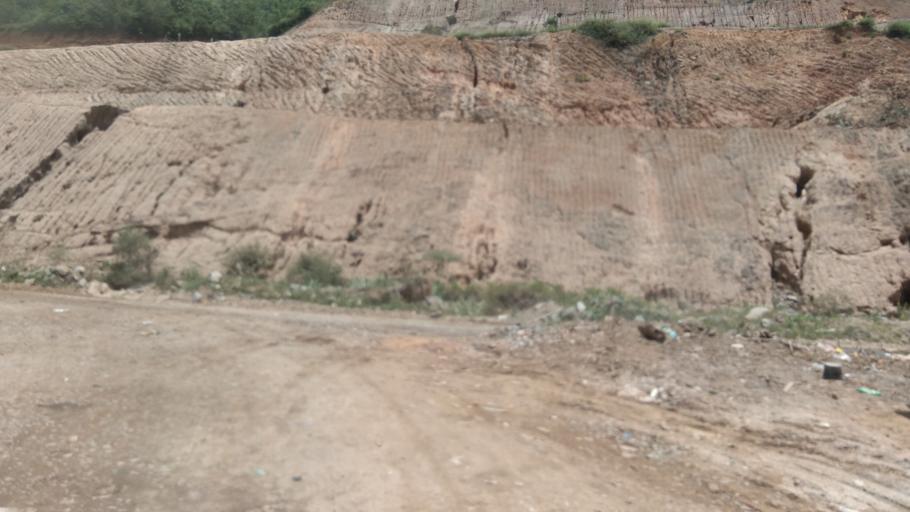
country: BR
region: Minas Gerais
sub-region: Santa Luzia
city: Santa Luzia
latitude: -19.8507
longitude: -43.8481
